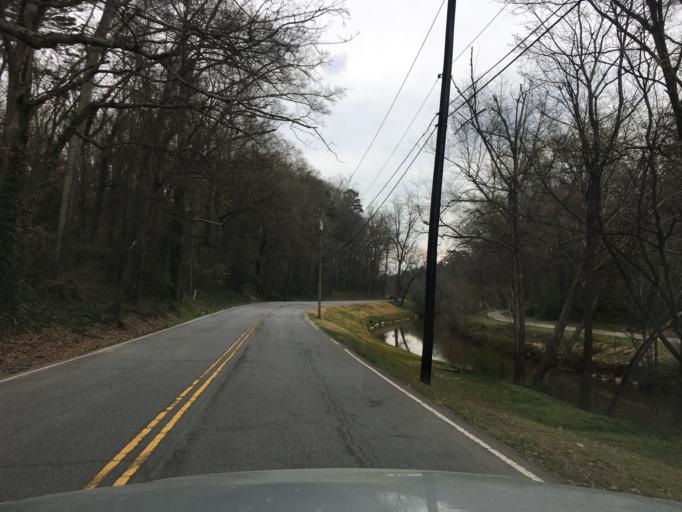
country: US
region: South Carolina
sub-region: Greenville County
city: Greenville
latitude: 34.8426
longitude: -82.3917
